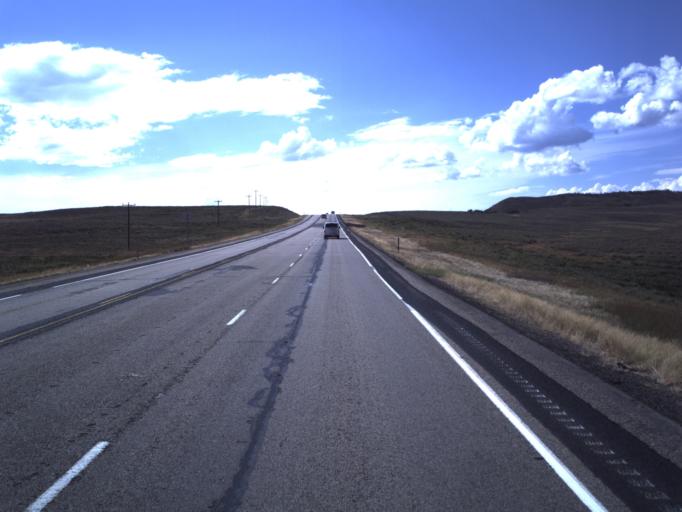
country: US
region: Utah
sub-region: Wasatch County
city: Heber
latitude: 40.1887
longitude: -111.0711
